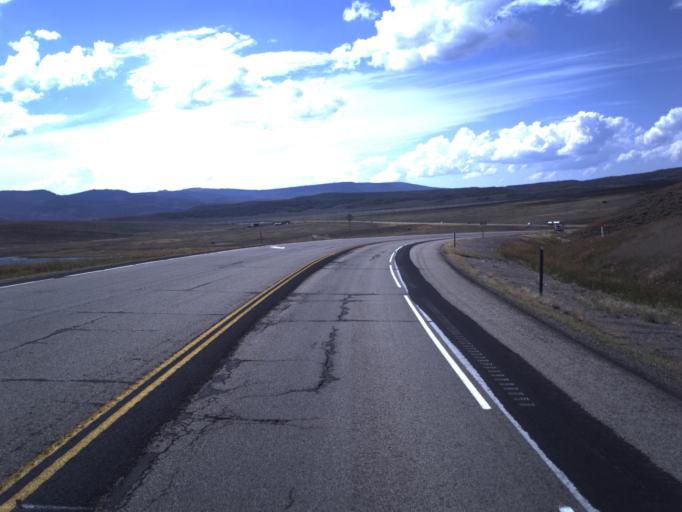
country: US
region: Utah
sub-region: Wasatch County
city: Heber
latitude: 40.2318
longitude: -111.1303
